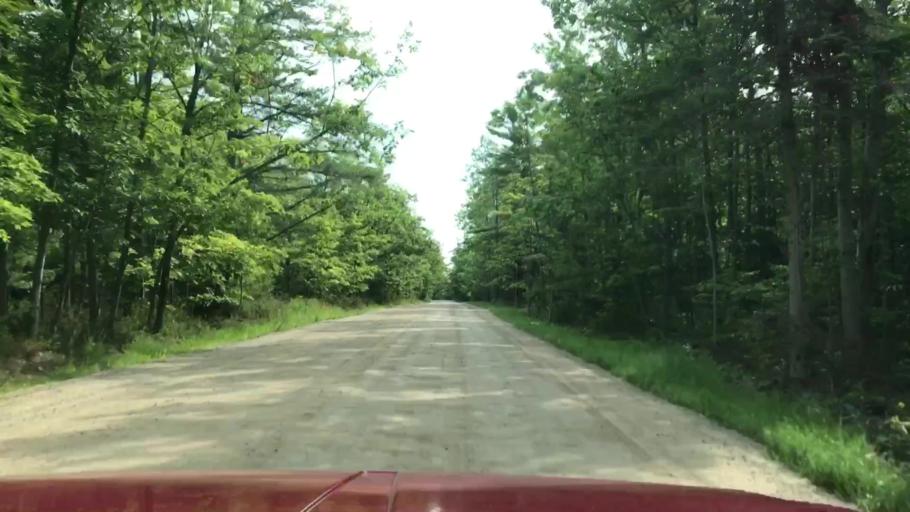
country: US
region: Michigan
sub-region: Charlevoix County
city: Charlevoix
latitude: 45.7468
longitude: -85.5294
